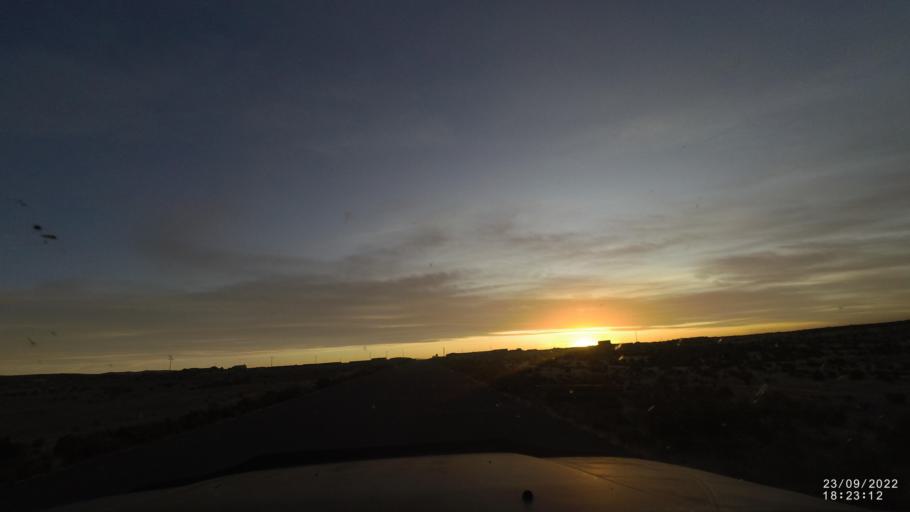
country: BO
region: Oruro
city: Challapata
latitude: -19.2937
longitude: -67.0995
